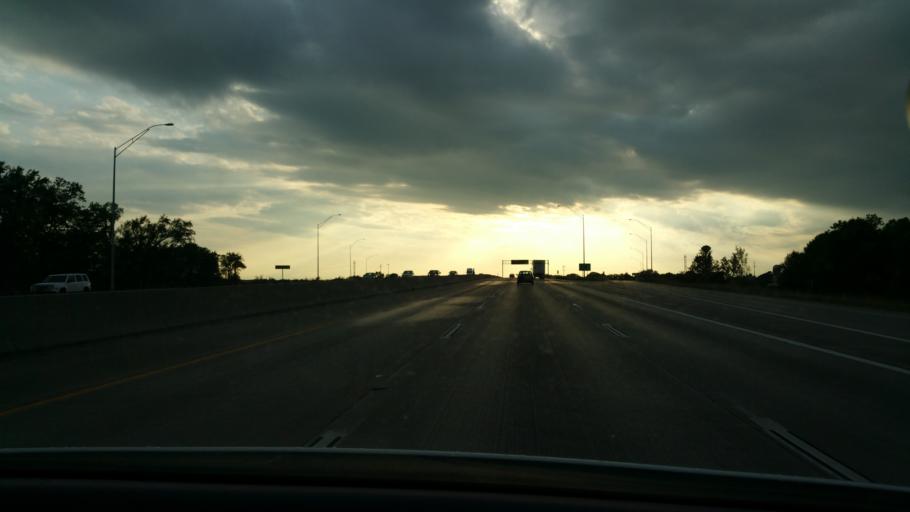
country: US
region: Iowa
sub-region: Polk County
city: Saylorville
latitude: 41.6495
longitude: -93.6122
